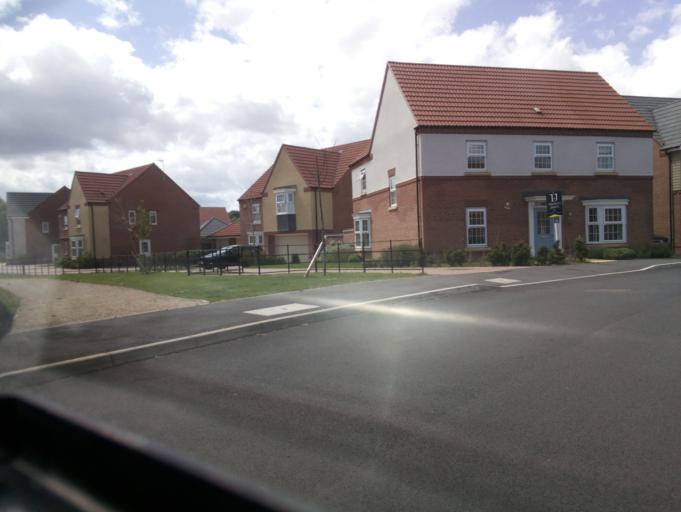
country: GB
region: England
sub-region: Nottinghamshire
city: Cotgrave
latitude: 52.9179
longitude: -1.0315
